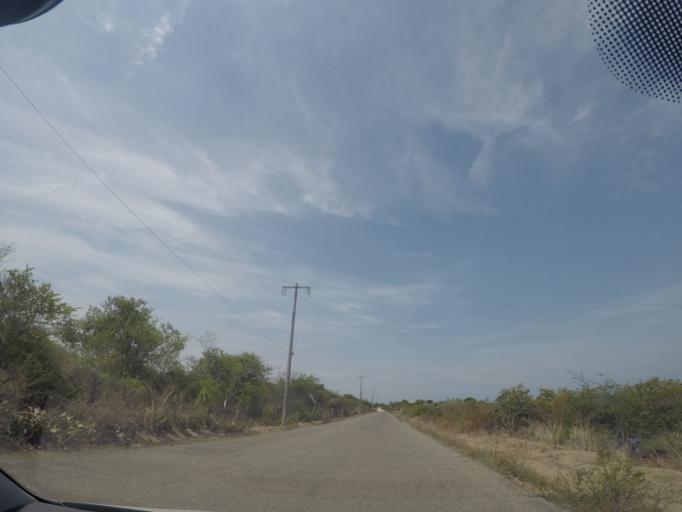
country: MX
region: Oaxaca
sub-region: Salina Cruz
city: Salina Cruz
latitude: 16.1950
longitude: -95.1193
